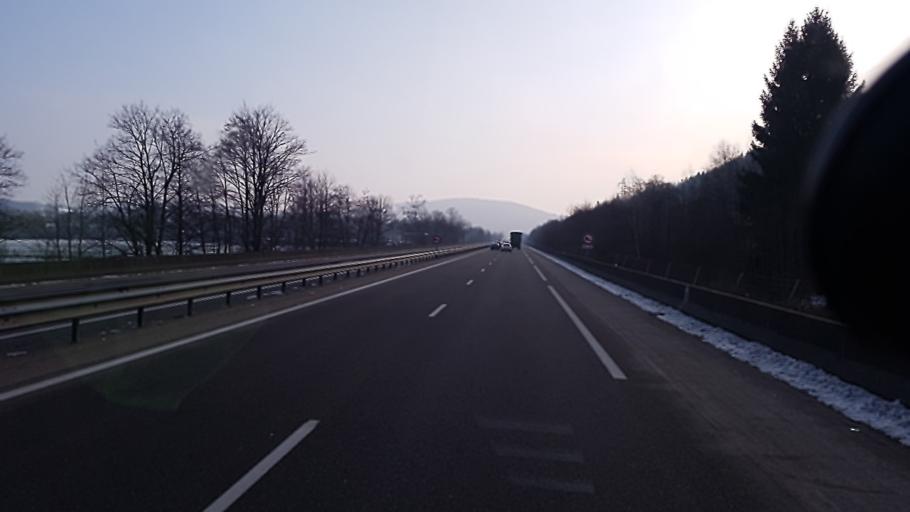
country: FR
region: Alsace
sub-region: Departement du Bas-Rhin
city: Urmatt
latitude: 48.5214
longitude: 7.3207
